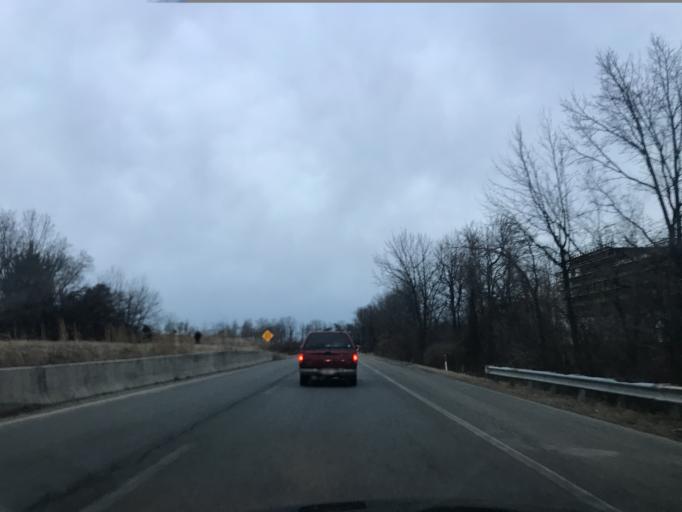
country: US
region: Maryland
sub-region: Prince George's County
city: Glenarden
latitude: 38.9183
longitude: -76.8496
